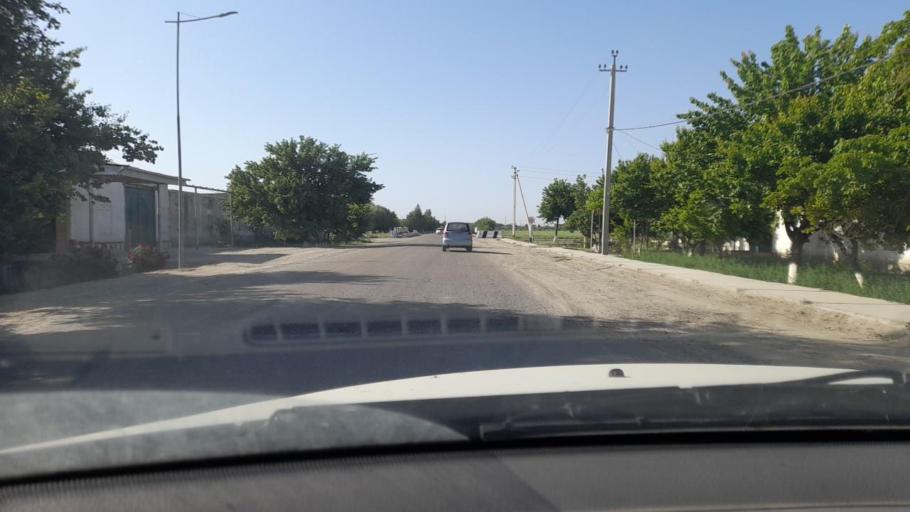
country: UZ
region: Bukhara
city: Romiton
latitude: 40.0730
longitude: 64.3265
